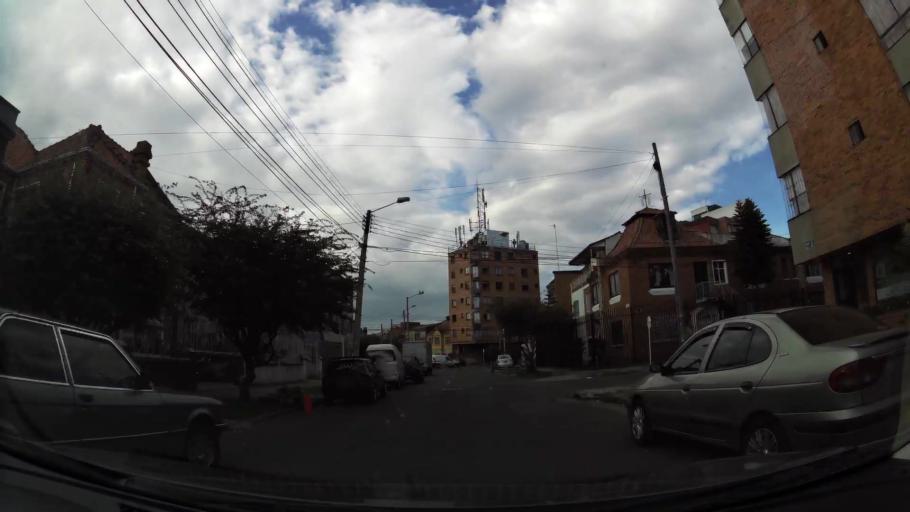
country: CO
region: Bogota D.C.
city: Bogota
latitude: 4.6462
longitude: -74.0704
